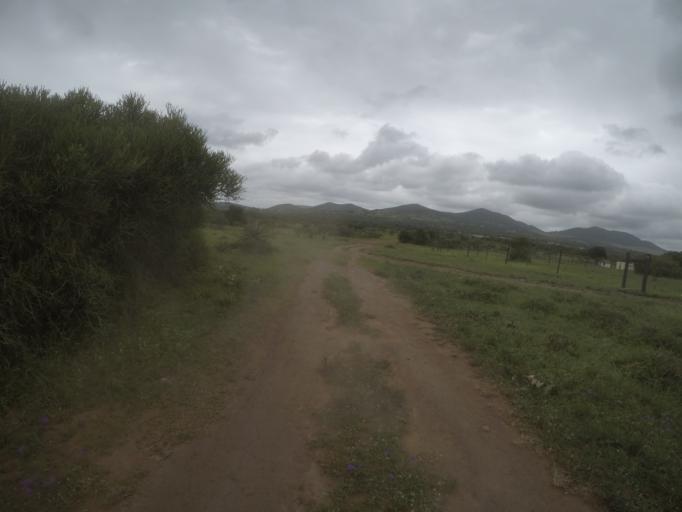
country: ZA
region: KwaZulu-Natal
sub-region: uThungulu District Municipality
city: Empangeni
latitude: -28.6105
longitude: 31.8614
